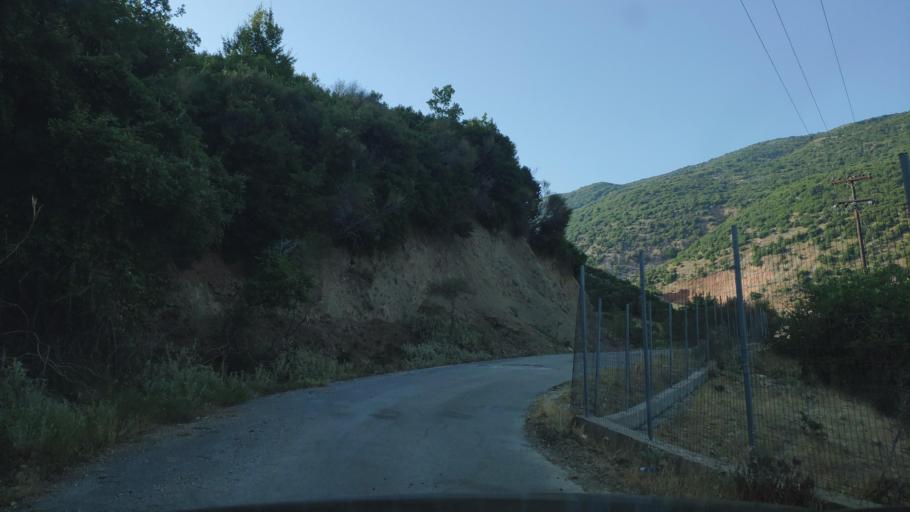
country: GR
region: West Greece
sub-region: Nomos Aitolias kai Akarnanias
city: Monastirakion
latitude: 38.8497
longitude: 20.9796
